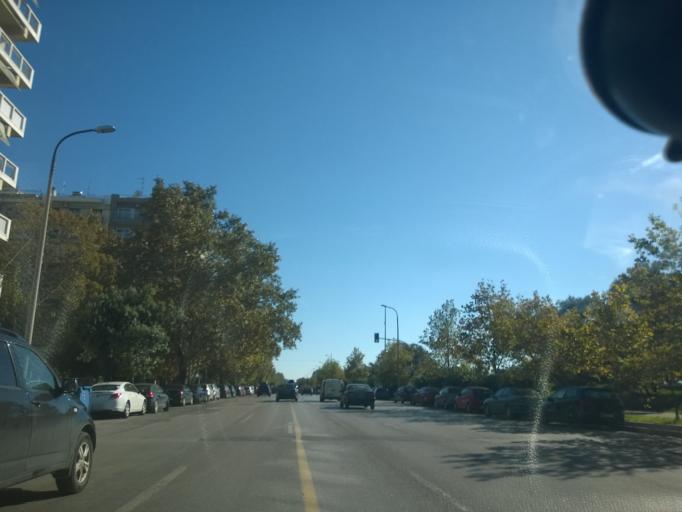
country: GR
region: Central Macedonia
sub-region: Nomos Thessalonikis
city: Triandria
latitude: 40.6149
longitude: 22.9526
